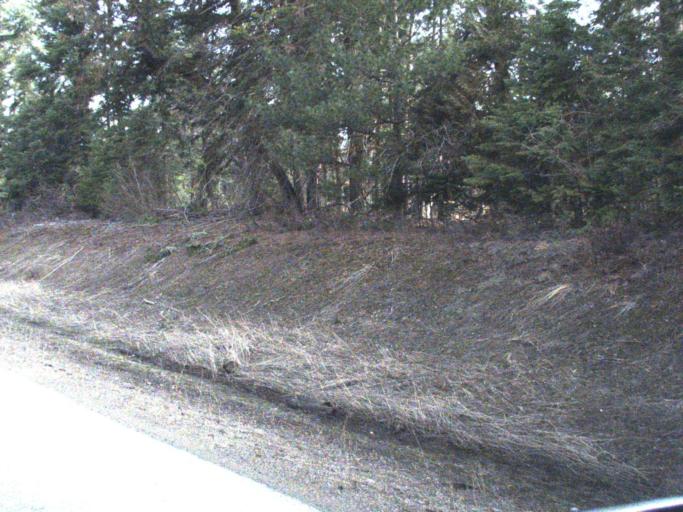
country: US
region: Washington
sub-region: Pend Oreille County
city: Newport
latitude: 48.2825
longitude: -117.2687
